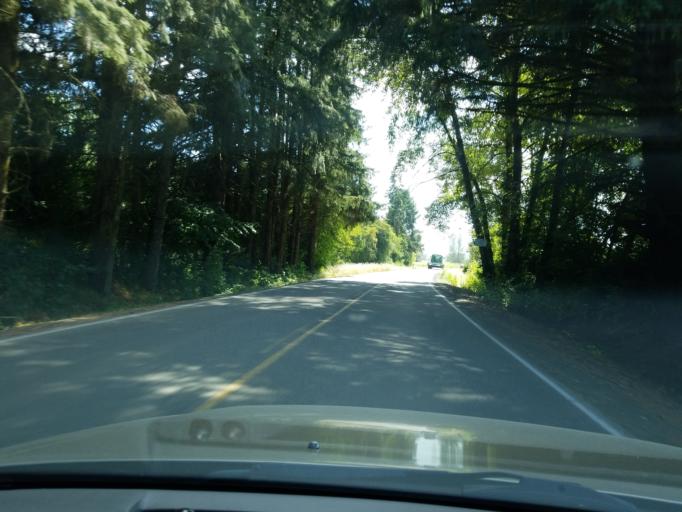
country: US
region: Oregon
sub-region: Yamhill County
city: Carlton
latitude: 45.2968
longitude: -123.1475
